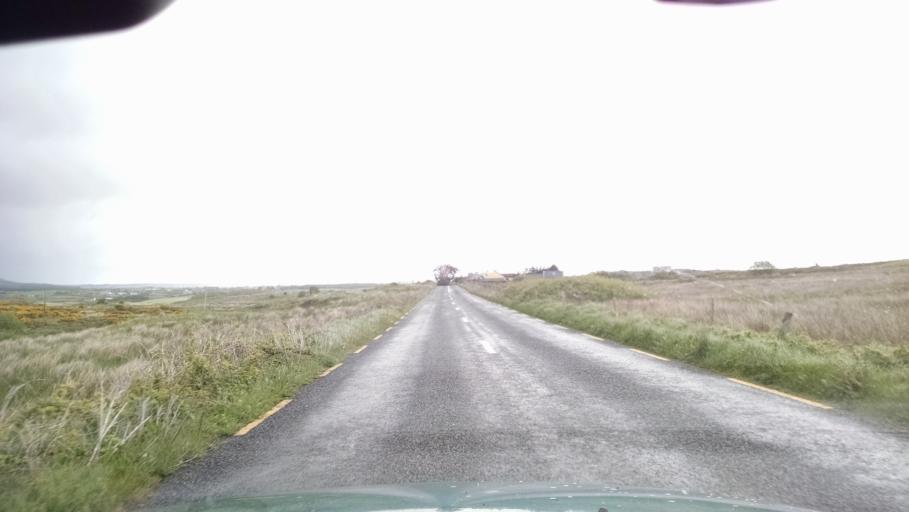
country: IE
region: Connaught
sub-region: County Galway
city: Bearna
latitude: 53.0135
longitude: -9.3321
